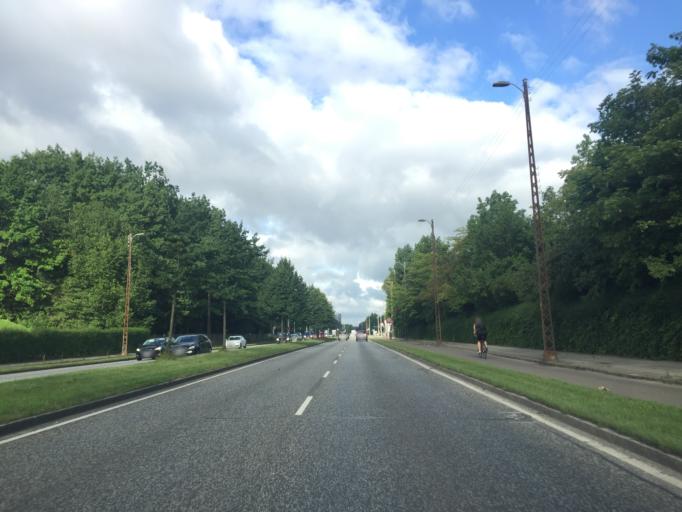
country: DK
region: Capital Region
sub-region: Rodovre Kommune
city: Rodovre
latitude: 55.6706
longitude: 12.4492
